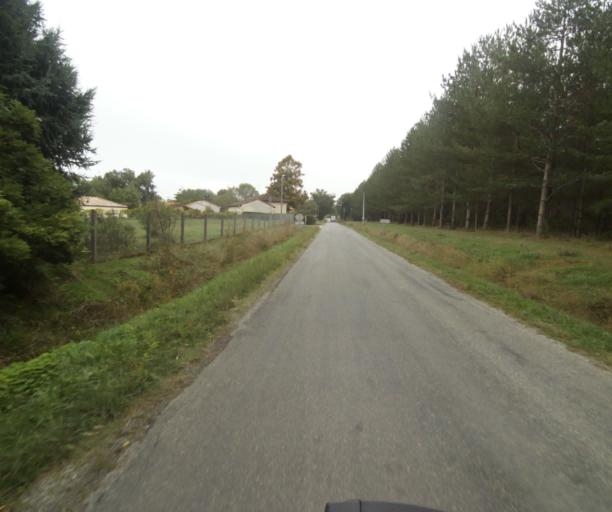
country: FR
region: Midi-Pyrenees
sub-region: Departement du Tarn-et-Garonne
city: Orgueil
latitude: 43.9011
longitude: 1.4019
